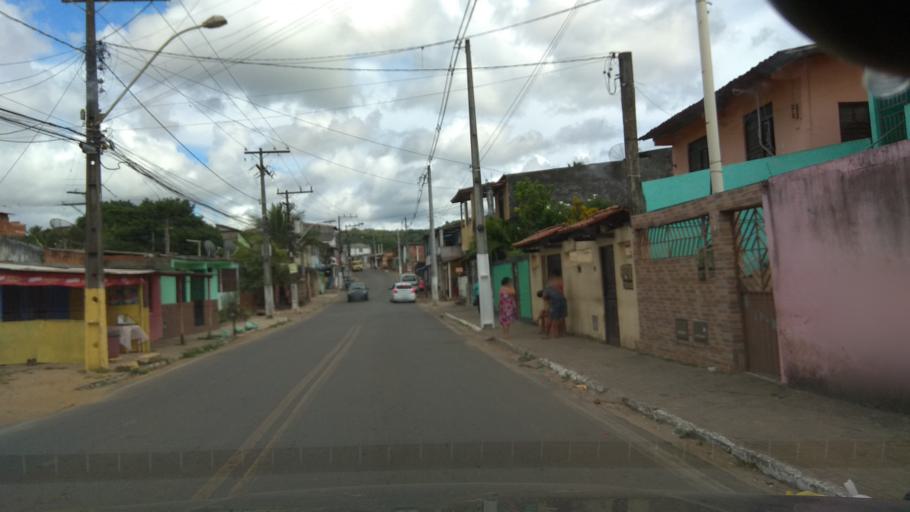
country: BR
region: Bahia
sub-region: Ilheus
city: Ilheus
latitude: -14.7843
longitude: -39.0579
